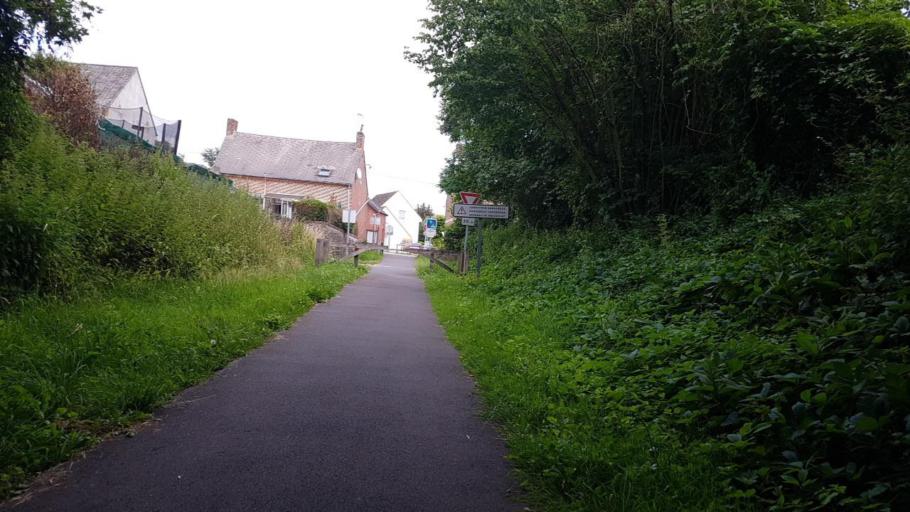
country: FR
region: Picardie
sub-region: Departement de l'Aisne
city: La Capelle
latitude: 49.9059
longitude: 3.9125
